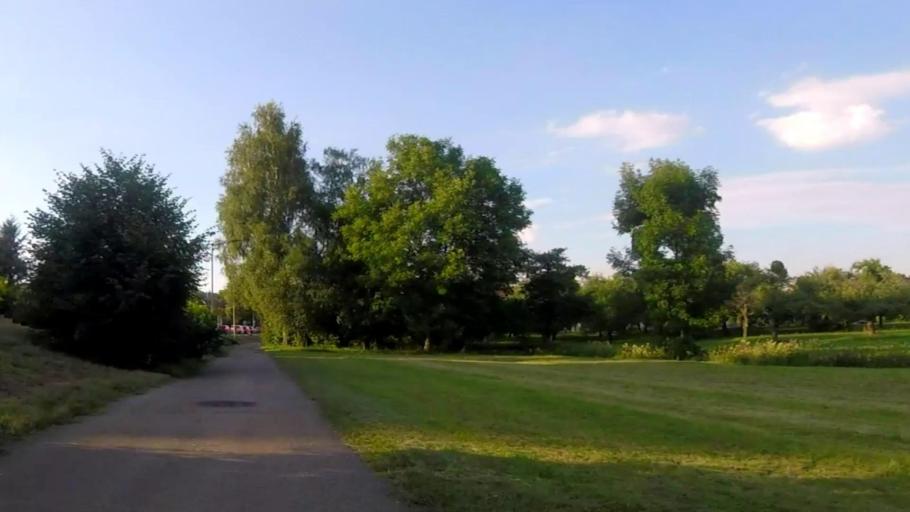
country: DE
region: Baden-Wuerttemberg
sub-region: Regierungsbezirk Stuttgart
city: Oppenweiler
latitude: 48.9716
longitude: 9.4384
